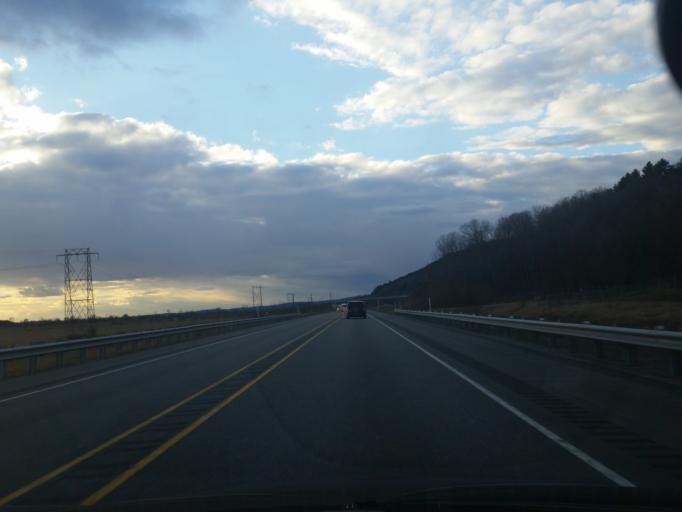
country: CA
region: Ontario
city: Hawkesbury
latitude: 45.6525
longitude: -74.7950
